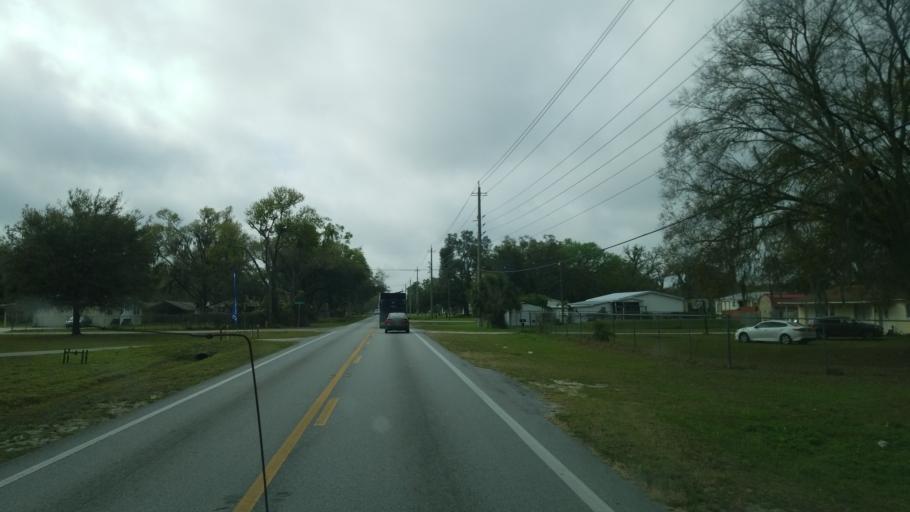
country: US
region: Florida
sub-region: Polk County
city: Kathleen
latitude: 28.0776
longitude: -82.0067
